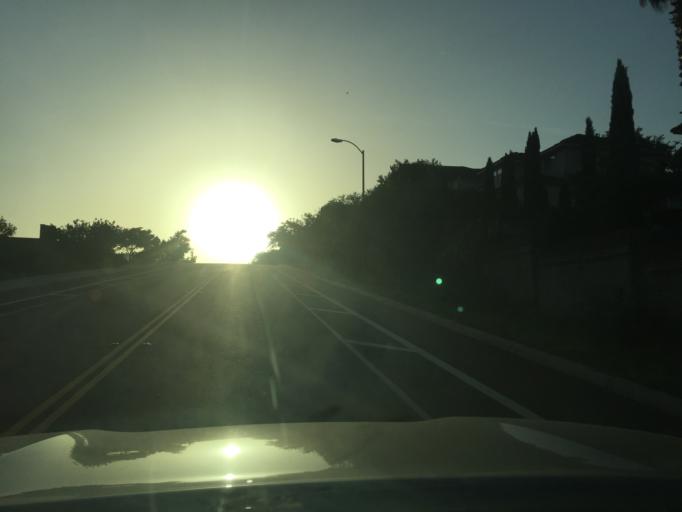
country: US
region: Texas
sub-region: Bexar County
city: Hollywood Park
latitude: 29.6320
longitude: -98.4928
